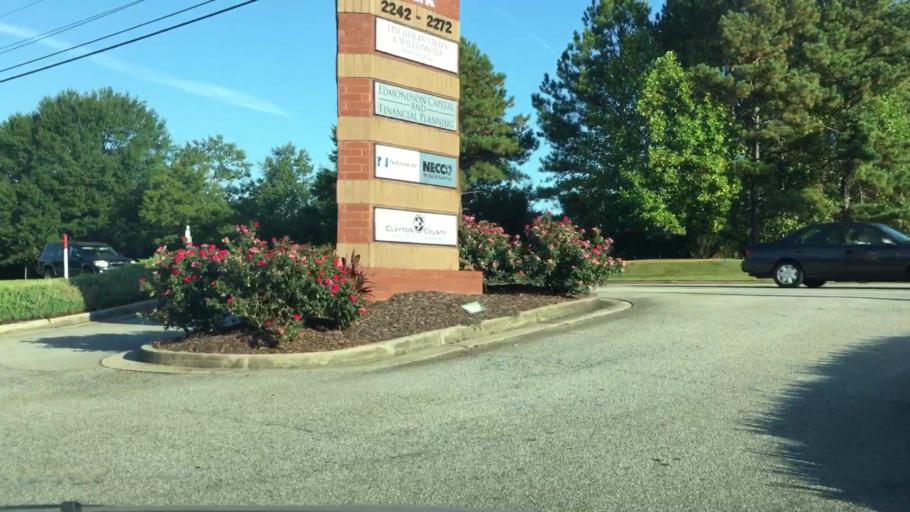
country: US
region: Georgia
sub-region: Clayton County
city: Morrow
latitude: 33.5600
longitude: -84.3165
